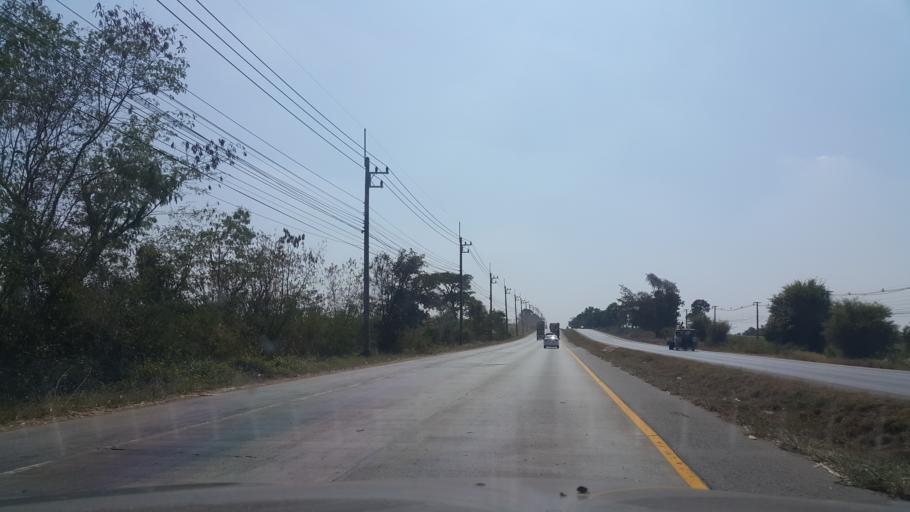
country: TH
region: Khon Kaen
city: Nam Phong
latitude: 16.8016
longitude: 102.8316
